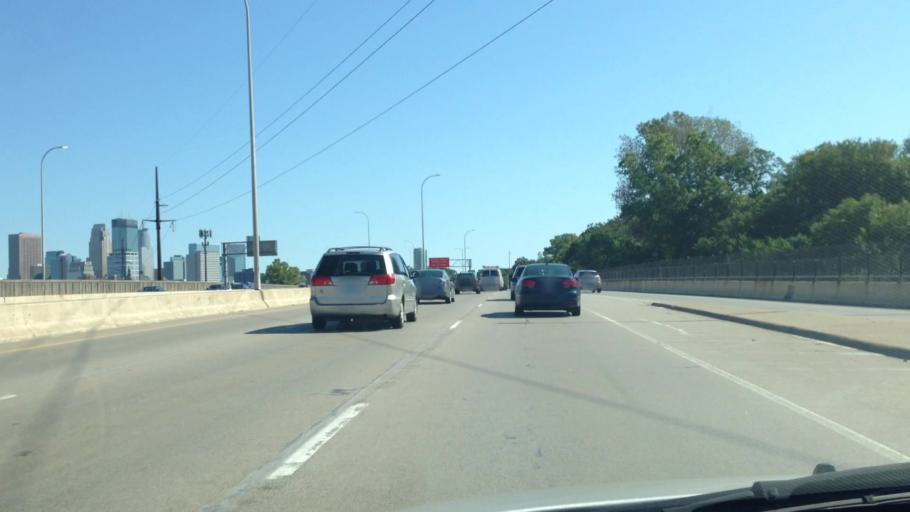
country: US
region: Minnesota
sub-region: Hennepin County
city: Minneapolis
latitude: 44.9694
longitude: -93.3061
